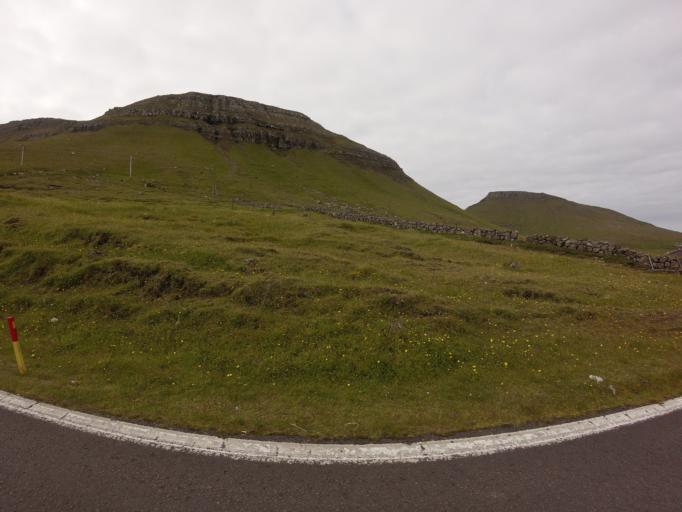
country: FO
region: Suduroy
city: Tvoroyri
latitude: 61.5943
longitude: -6.9501
